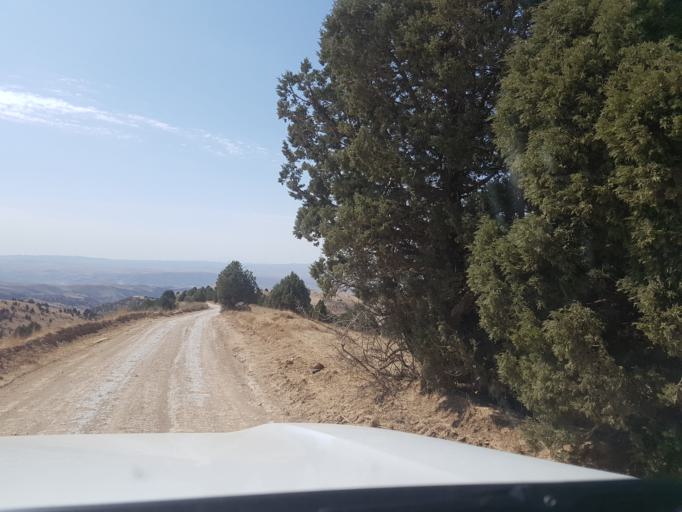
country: TM
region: Ahal
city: Baharly
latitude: 38.3098
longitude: 56.9497
